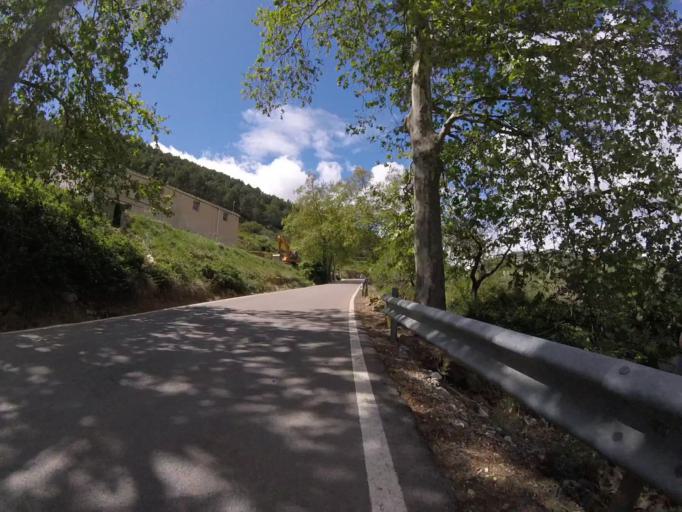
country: ES
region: Valencia
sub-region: Provincia de Castello
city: Sierra-Engarceran
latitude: 40.2710
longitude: -0.0133
